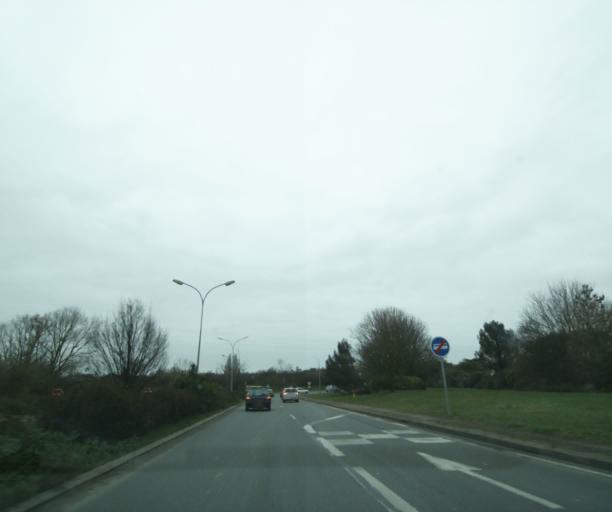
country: FR
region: Poitou-Charentes
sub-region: Departement de la Charente-Maritime
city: Lagord
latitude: 46.1812
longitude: -1.1528
